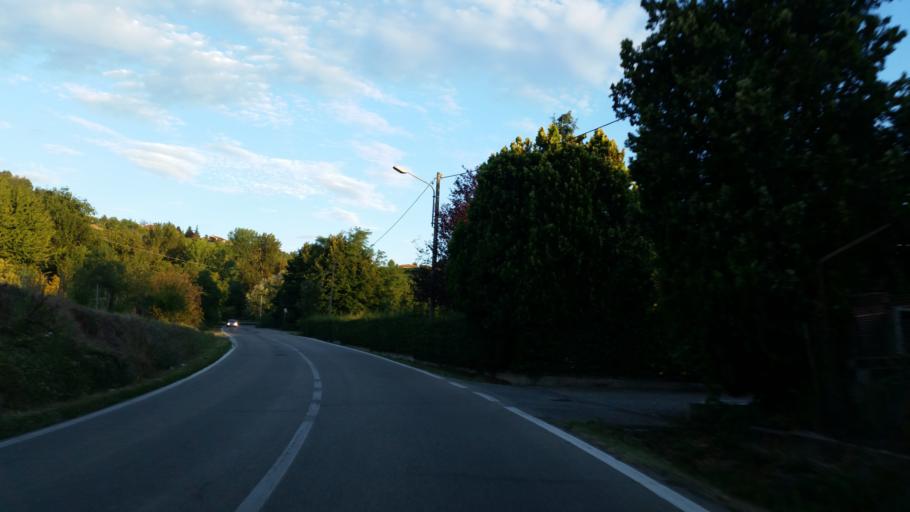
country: IT
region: Piedmont
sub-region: Provincia di Asti
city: Costigliole d'Asti
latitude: 44.7981
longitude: 8.1822
